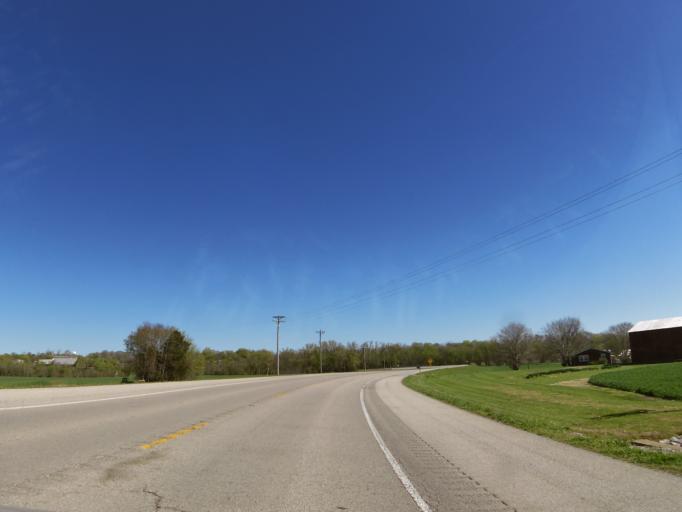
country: US
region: Tennessee
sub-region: Robertson County
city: Springfield
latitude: 36.6563
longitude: -86.8535
